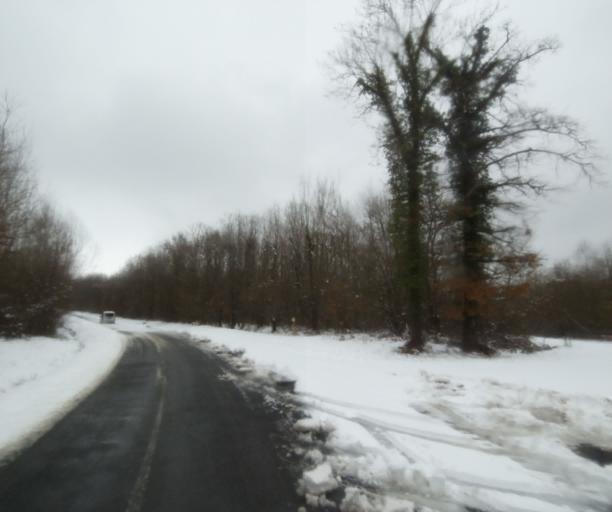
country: FR
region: Champagne-Ardenne
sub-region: Departement de la Haute-Marne
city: Laneuville-a-Remy
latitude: 48.5100
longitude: 4.8975
